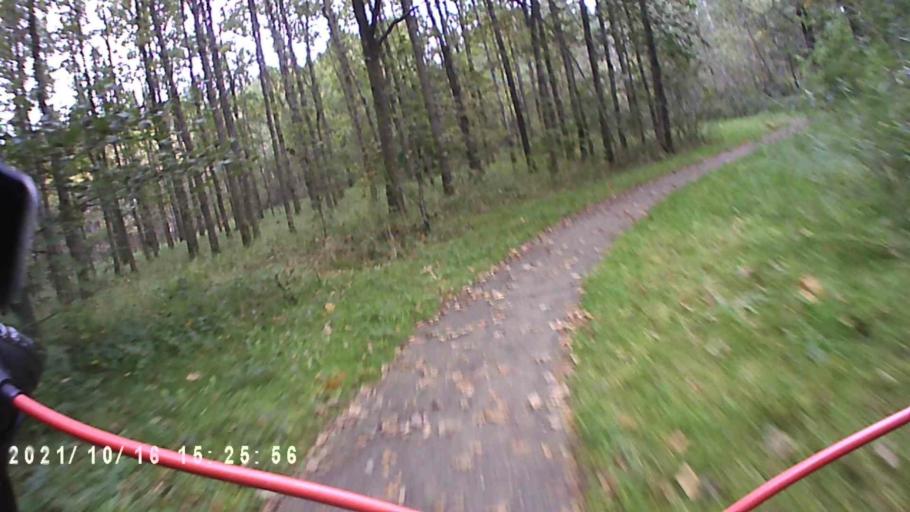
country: NL
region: Friesland
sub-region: Gemeente Dongeradeel
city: Anjum
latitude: 53.3995
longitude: 6.2296
